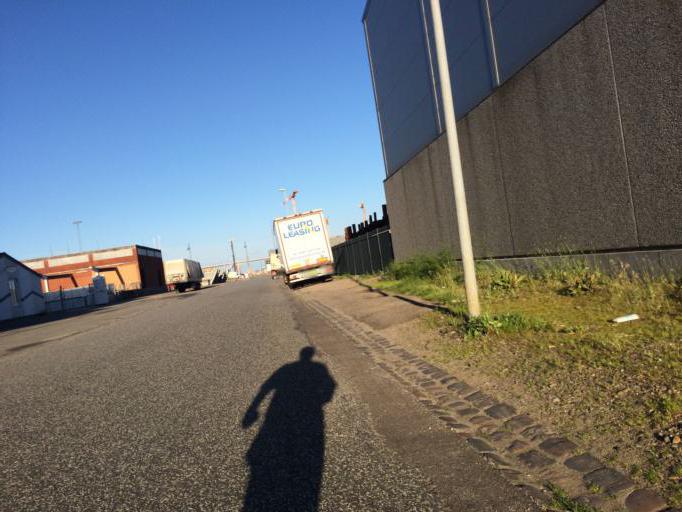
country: DK
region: South Denmark
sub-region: Vejle Kommune
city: Vejle
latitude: 55.7075
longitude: 9.5482
